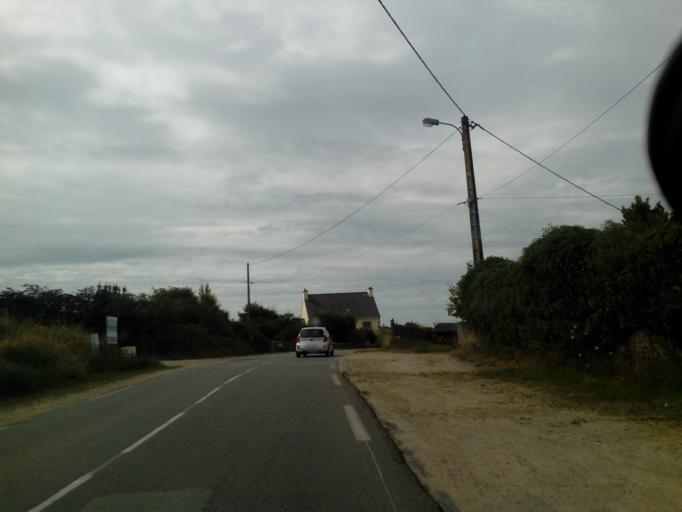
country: FR
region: Brittany
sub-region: Departement du Morbihan
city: Erdeven
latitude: 47.6224
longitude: -3.1617
